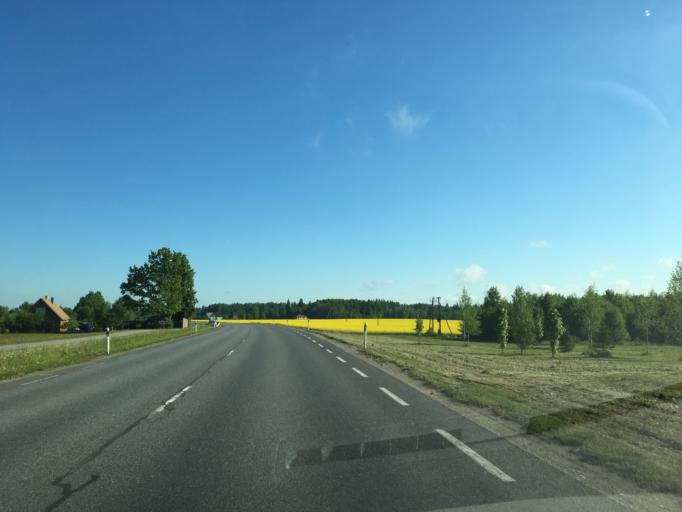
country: EE
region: Tartu
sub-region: Tartu linn
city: Tartu
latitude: 58.4393
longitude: 26.6817
